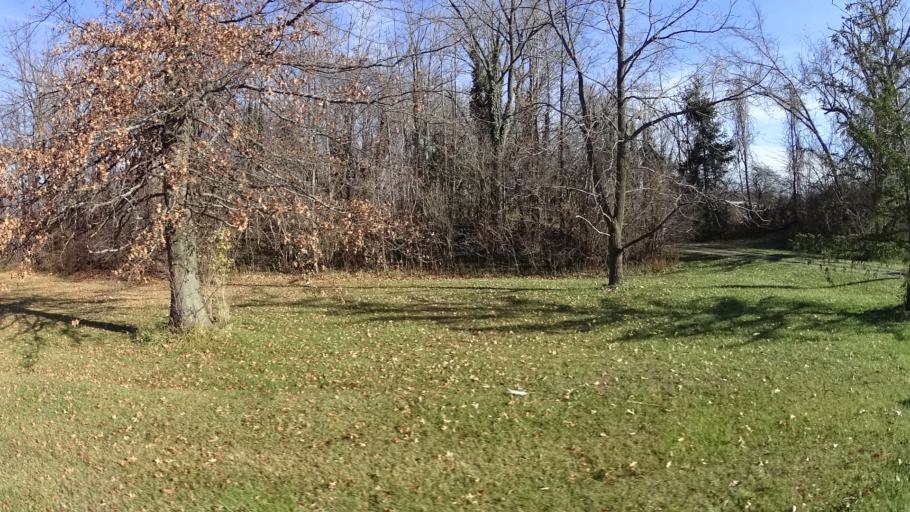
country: US
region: Ohio
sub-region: Lorain County
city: Wellington
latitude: 41.1132
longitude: -82.2391
